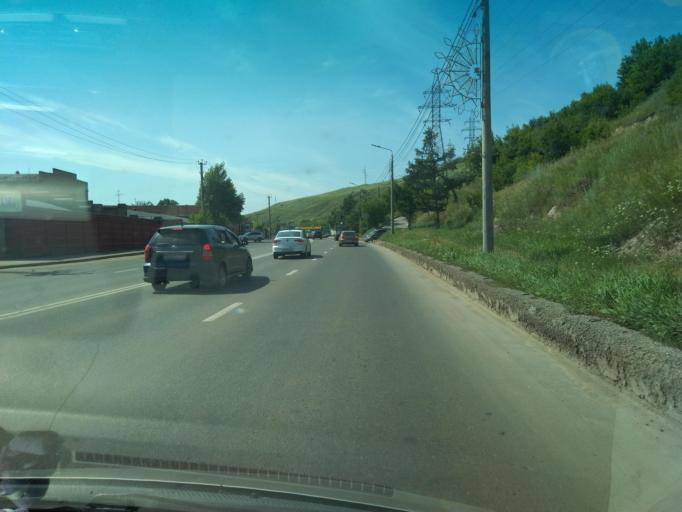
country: RU
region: Krasnoyarskiy
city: Krasnoyarsk
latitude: 56.0205
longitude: 92.8728
